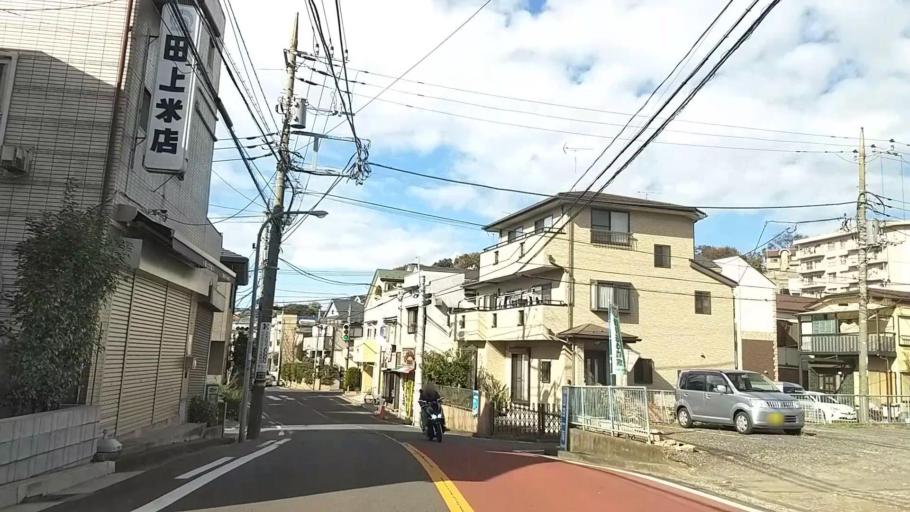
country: JP
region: Kanagawa
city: Yokohama
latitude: 35.5051
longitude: 139.6582
